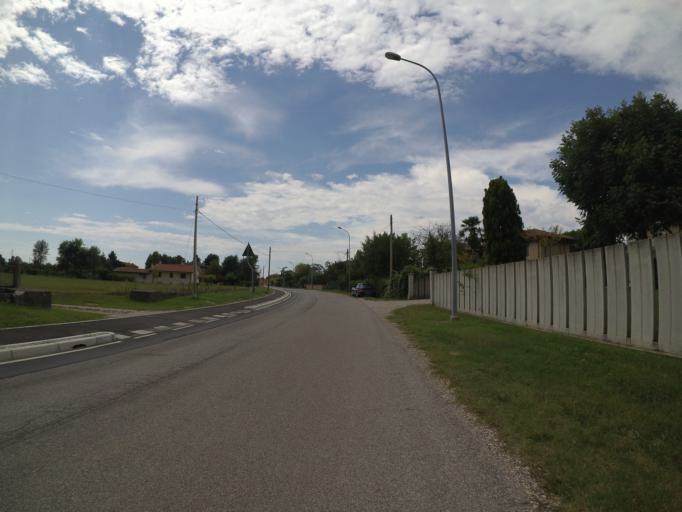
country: IT
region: Friuli Venezia Giulia
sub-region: Provincia di Udine
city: Talmassons
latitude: 45.9217
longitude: 13.1480
